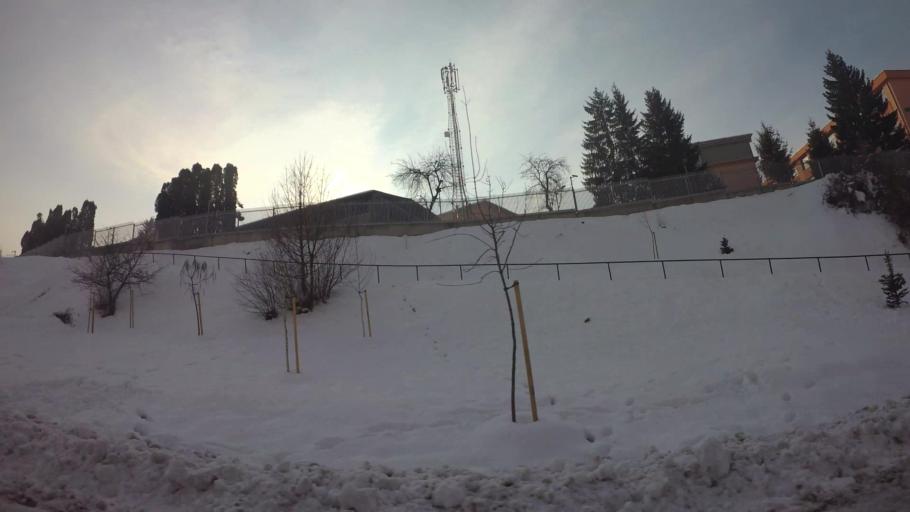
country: BA
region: Federation of Bosnia and Herzegovina
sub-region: Kanton Sarajevo
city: Sarajevo
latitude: 43.8451
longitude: 18.3680
